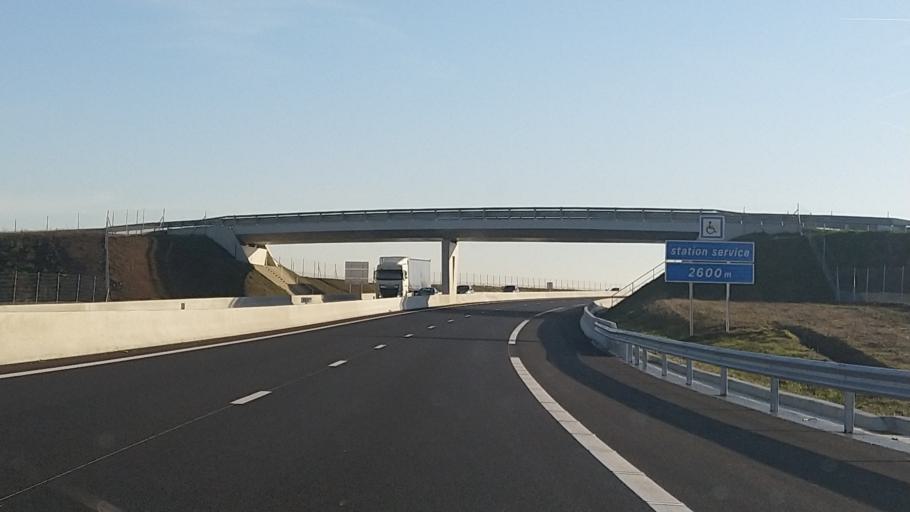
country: FR
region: Ile-de-France
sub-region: Departement du Val-d'Oise
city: Montsoult
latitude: 49.0791
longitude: 2.3301
